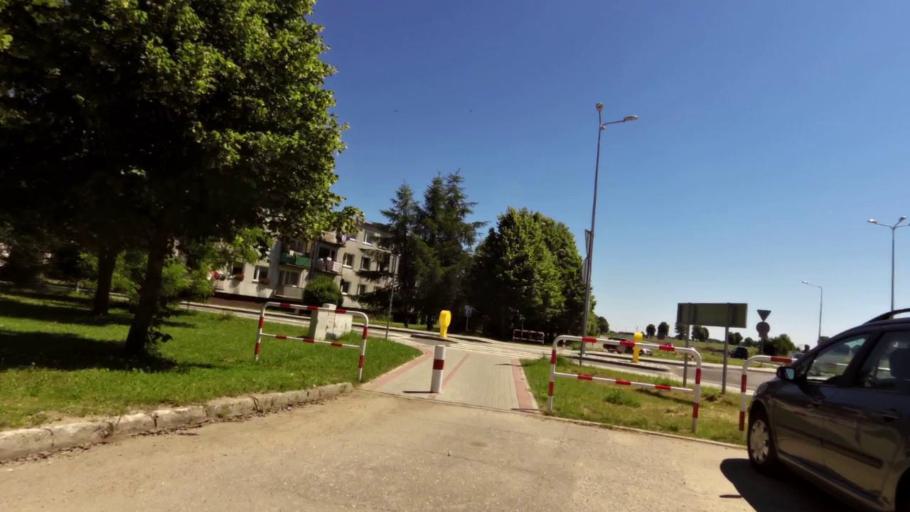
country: PL
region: West Pomeranian Voivodeship
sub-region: Powiat kolobrzeski
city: Goscino
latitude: 54.0500
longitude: 15.6477
